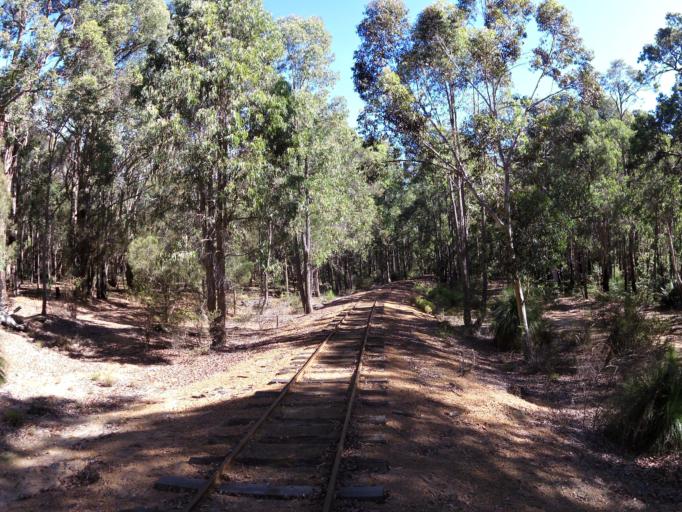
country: AU
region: Western Australia
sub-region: Waroona
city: Waroona
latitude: -32.7112
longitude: 116.0771
